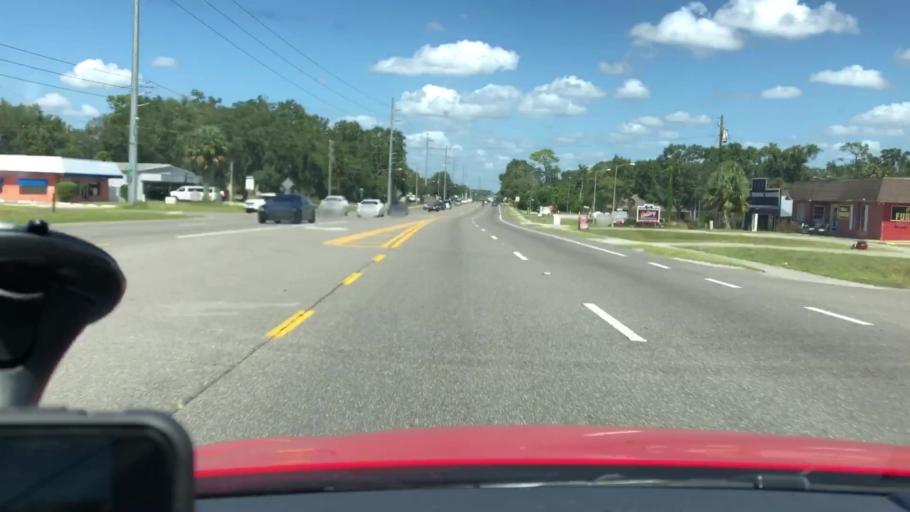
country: US
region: Florida
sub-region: Volusia County
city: Orange City
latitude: 28.9287
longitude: -81.2988
